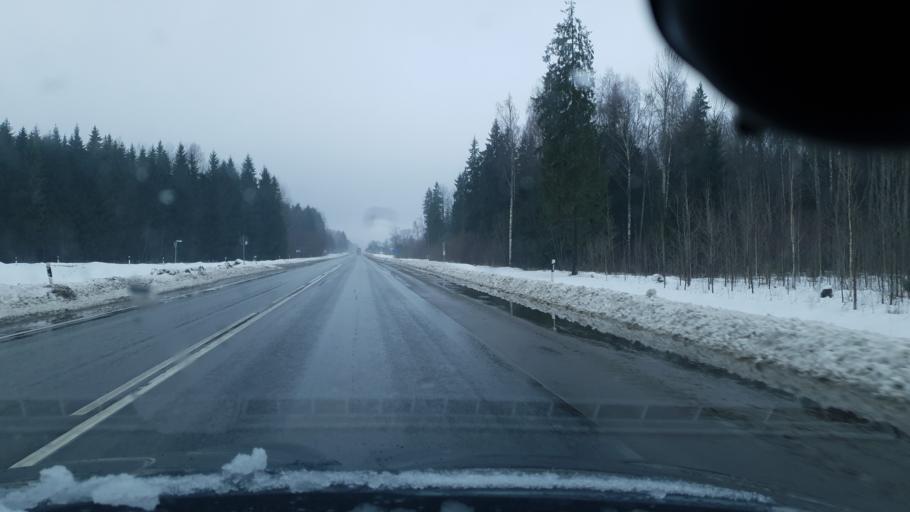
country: EE
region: Tartu
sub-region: Tartu linn
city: Tartu
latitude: 58.4127
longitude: 26.5872
